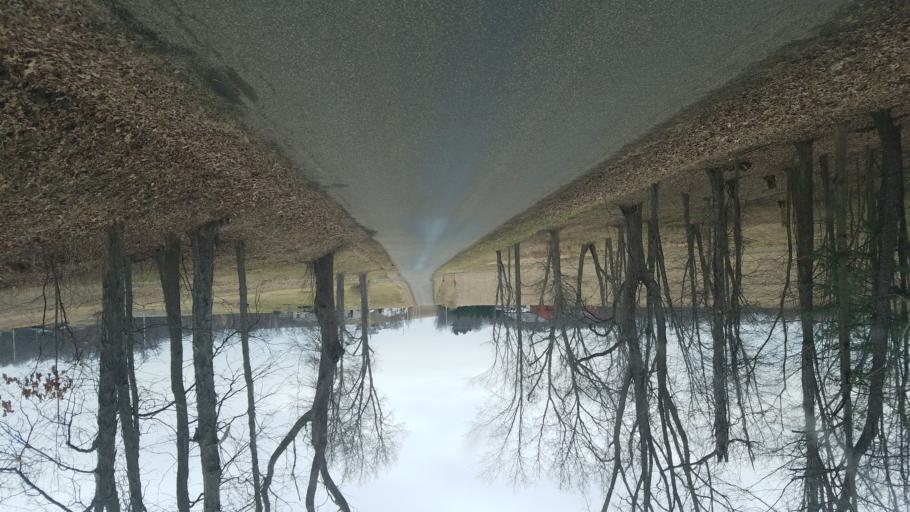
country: US
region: Ohio
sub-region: Ashland County
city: Loudonville
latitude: 40.6980
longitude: -82.2588
